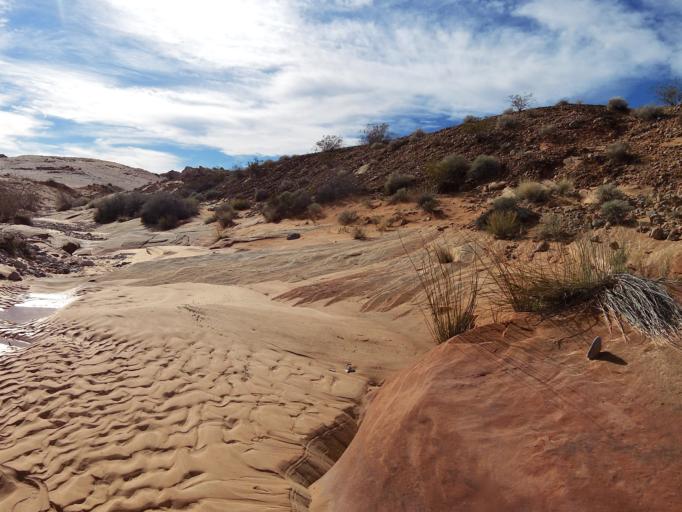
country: US
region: Nevada
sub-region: Clark County
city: Moapa Valley
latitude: 36.4819
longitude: -114.5227
